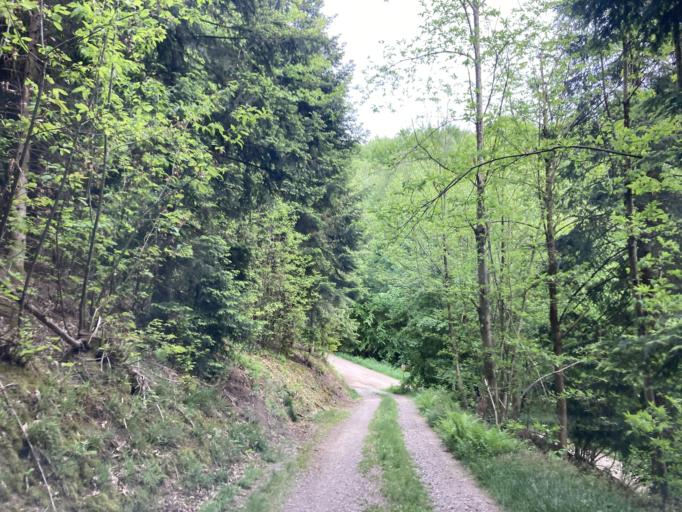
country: DE
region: Baden-Wuerttemberg
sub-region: Freiburg Region
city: Kappelrodeck
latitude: 48.6117
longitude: 8.1035
